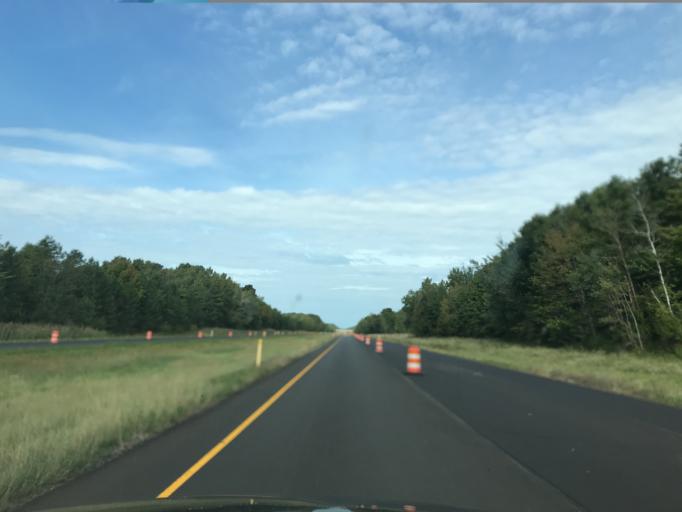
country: US
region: Ohio
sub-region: Ashtabula County
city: Jefferson
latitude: 41.7696
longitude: -80.7240
